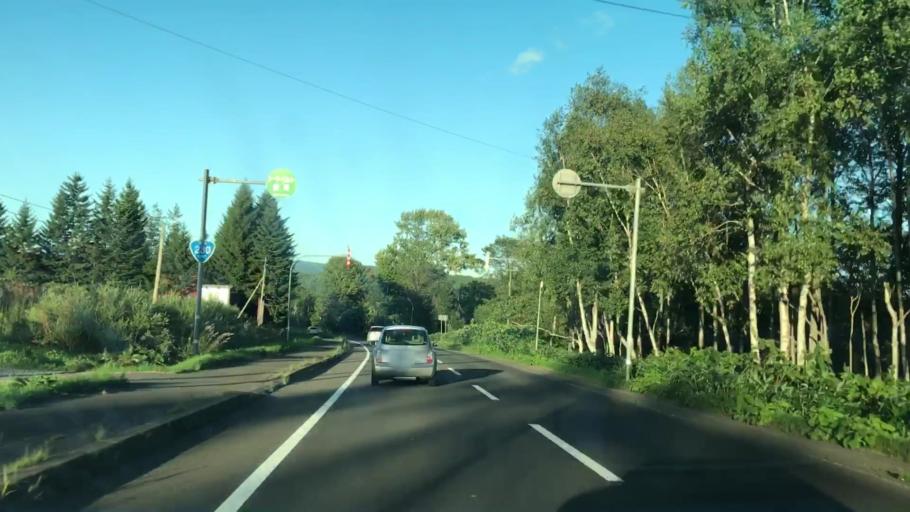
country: JP
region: Hokkaido
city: Niseko Town
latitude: 42.7535
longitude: 140.9175
